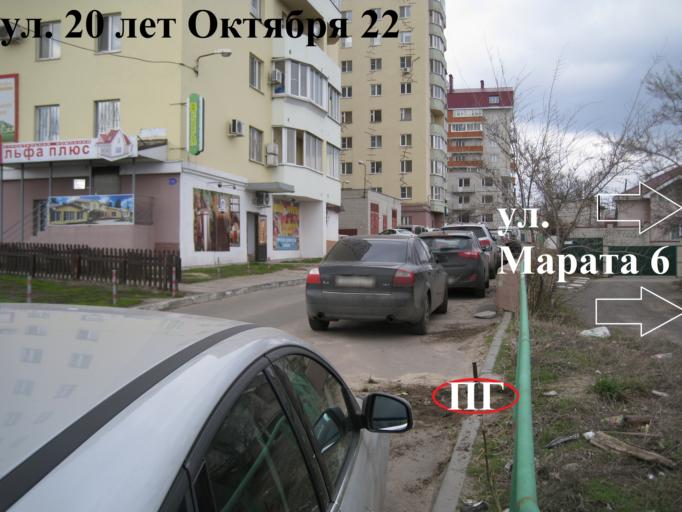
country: RU
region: Voronezj
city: Voronezh
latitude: 51.6413
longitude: 39.2044
